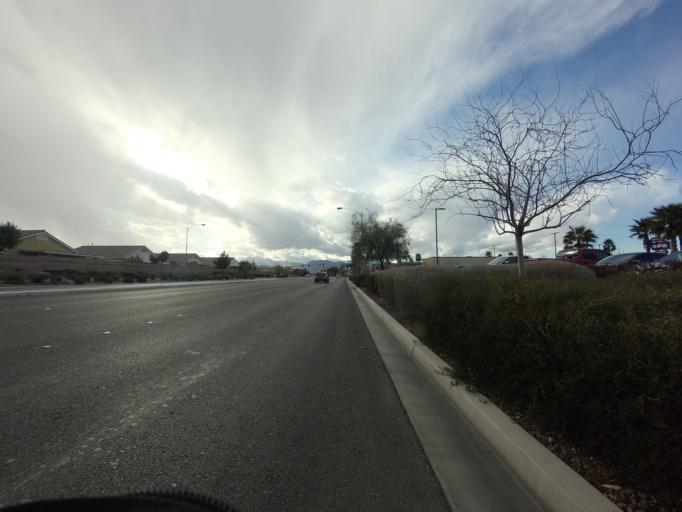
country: US
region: Nevada
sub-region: Clark County
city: North Las Vegas
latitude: 36.2691
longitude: -115.2049
